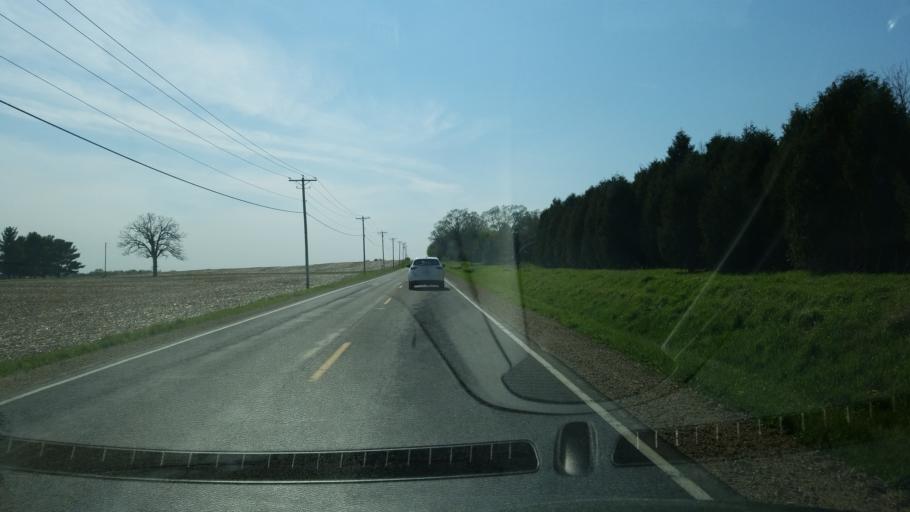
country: US
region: Wisconsin
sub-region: Dane County
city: Oregon
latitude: 42.9291
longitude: -89.4140
